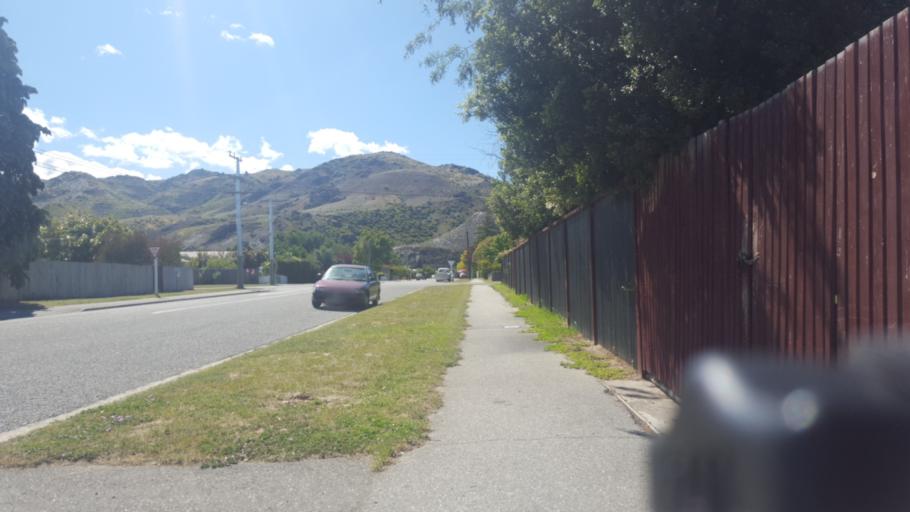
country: NZ
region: Otago
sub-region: Queenstown-Lakes District
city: Wanaka
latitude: -45.0472
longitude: 169.2073
